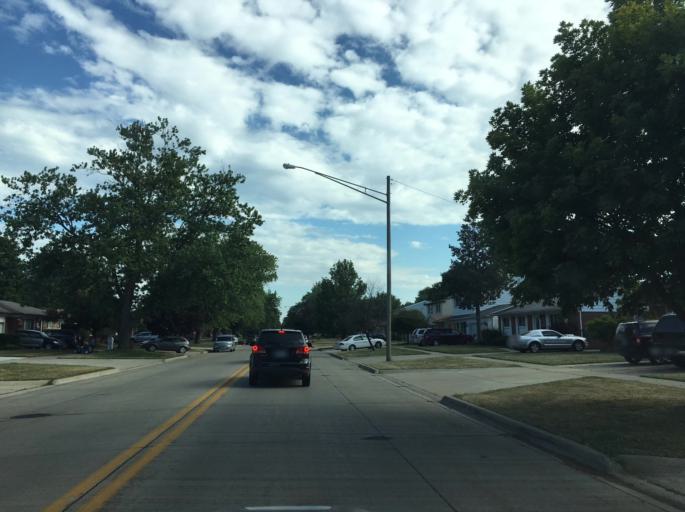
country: US
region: Michigan
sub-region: Macomb County
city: Fraser
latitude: 42.5350
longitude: -82.9295
